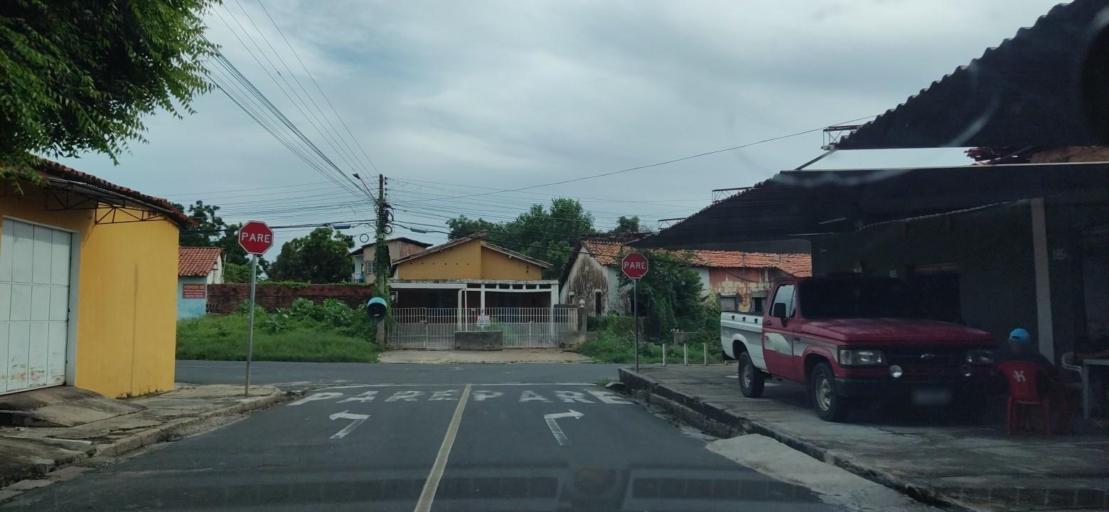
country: BR
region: Piaui
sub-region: Teresina
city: Teresina
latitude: -5.0975
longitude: -42.7988
